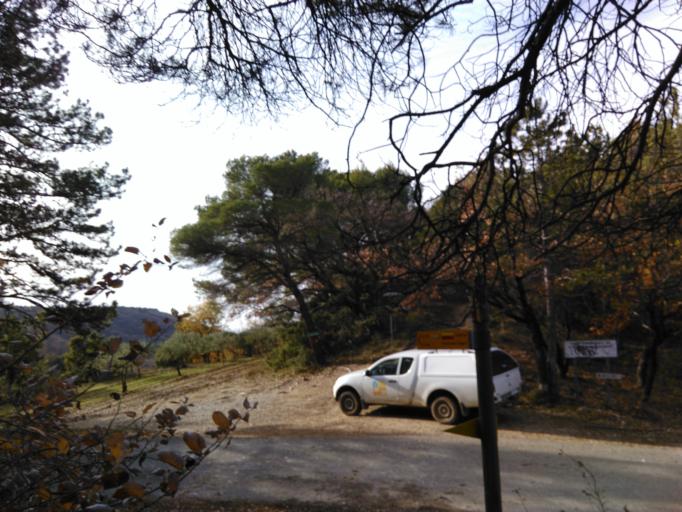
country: FR
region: Rhone-Alpes
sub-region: Departement de la Drome
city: Tulette
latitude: 44.2594
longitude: 4.9642
